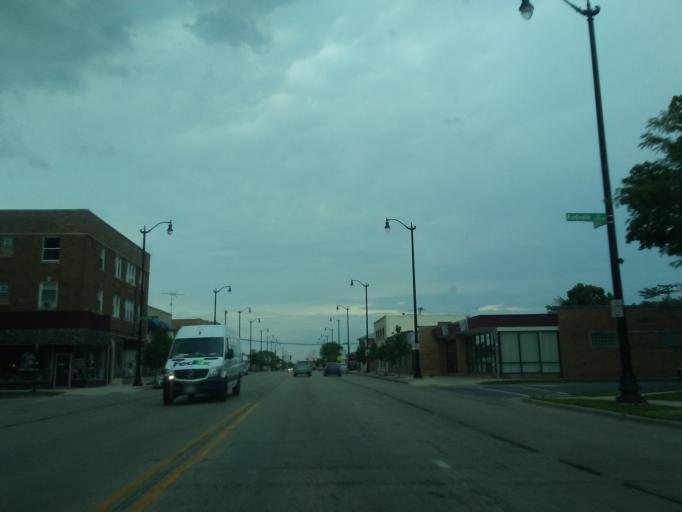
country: US
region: Illinois
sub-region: Cook County
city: Skokie
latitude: 42.0263
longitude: -87.7321
